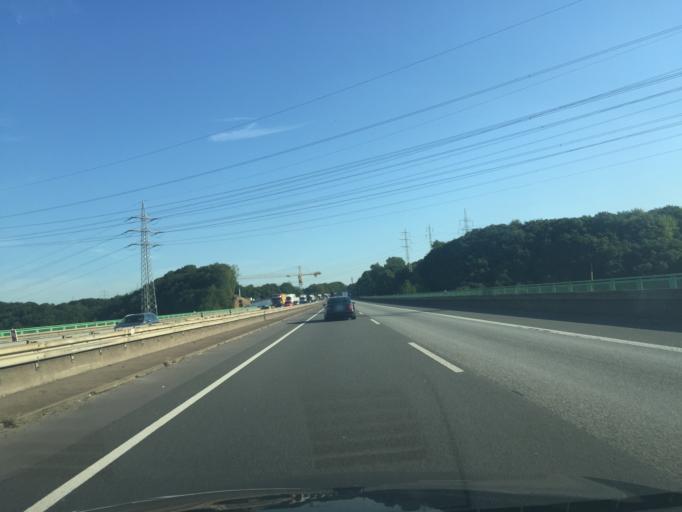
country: DE
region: North Rhine-Westphalia
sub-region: Regierungsbezirk Arnsberg
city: Hagen
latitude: 51.3854
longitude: 7.5253
